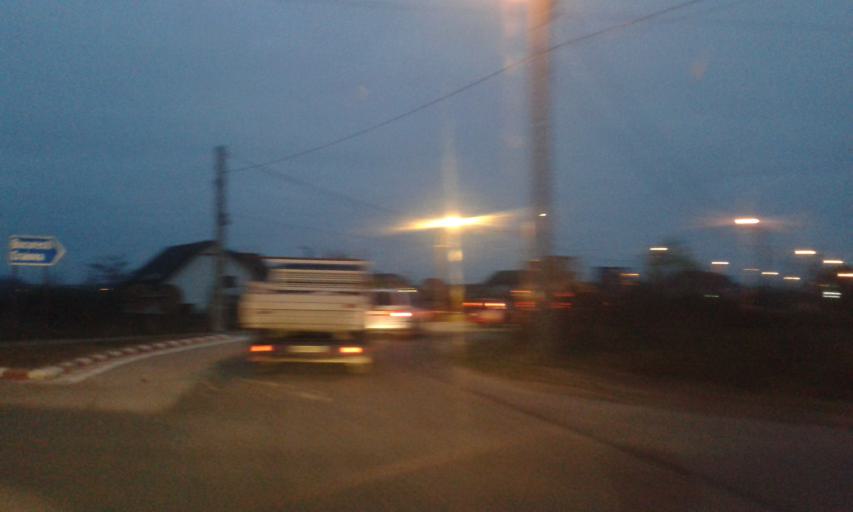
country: RO
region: Gorj
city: Targu Jiu
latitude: 45.0522
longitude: 23.2614
